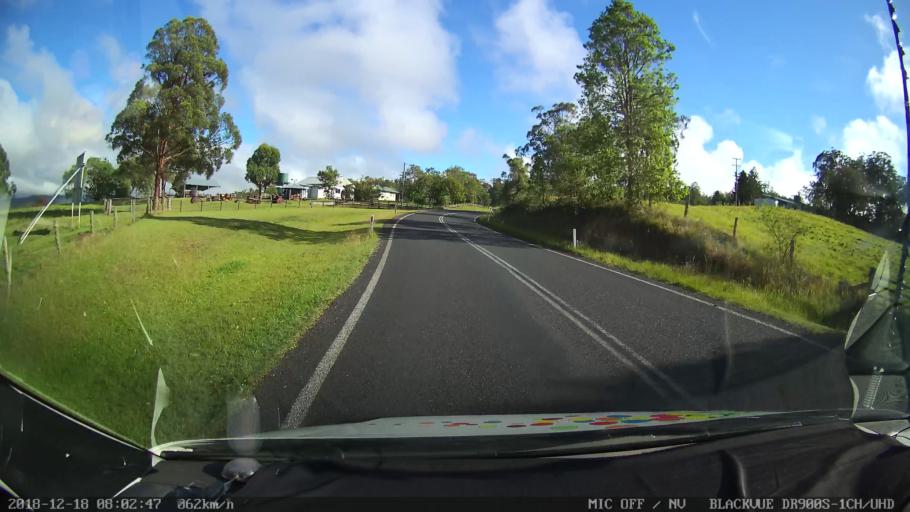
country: AU
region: New South Wales
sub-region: Kyogle
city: Kyogle
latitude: -28.3907
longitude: 152.6361
